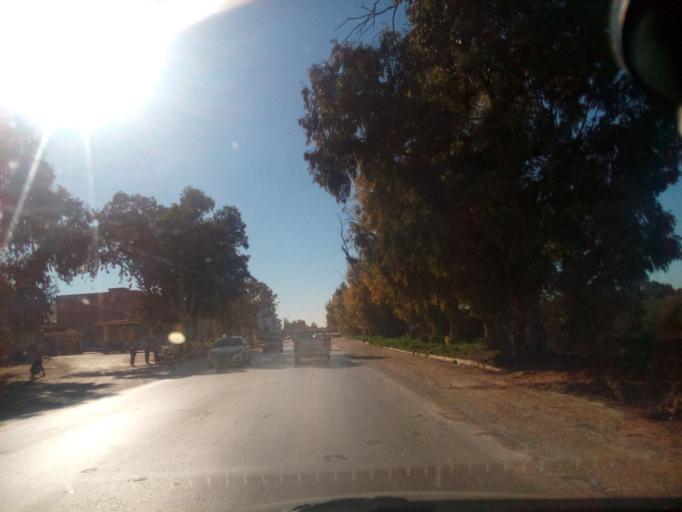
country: DZ
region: Relizane
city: Djidiouia
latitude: 35.9111
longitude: 0.7814
